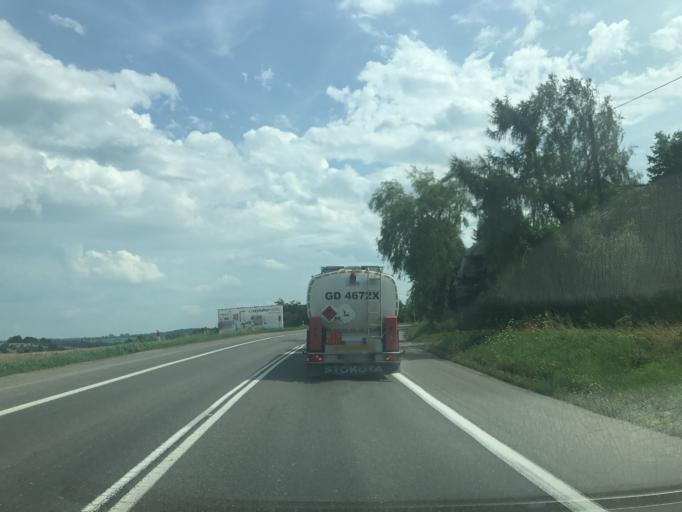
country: PL
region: Warmian-Masurian Voivodeship
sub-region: Powiat ostrodzki
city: Ostroda
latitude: 53.6627
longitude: 20.0445
